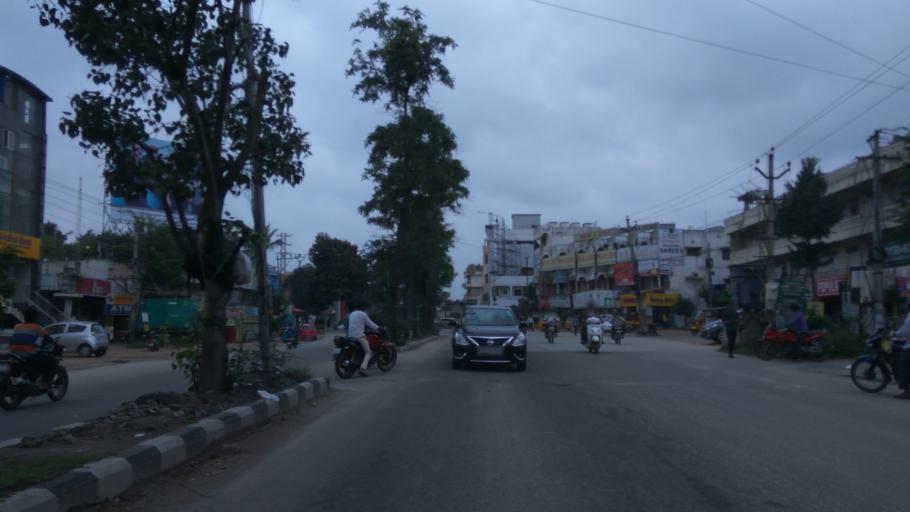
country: IN
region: Telangana
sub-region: Rangareddi
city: Secunderabad
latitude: 17.4793
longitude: 78.5588
